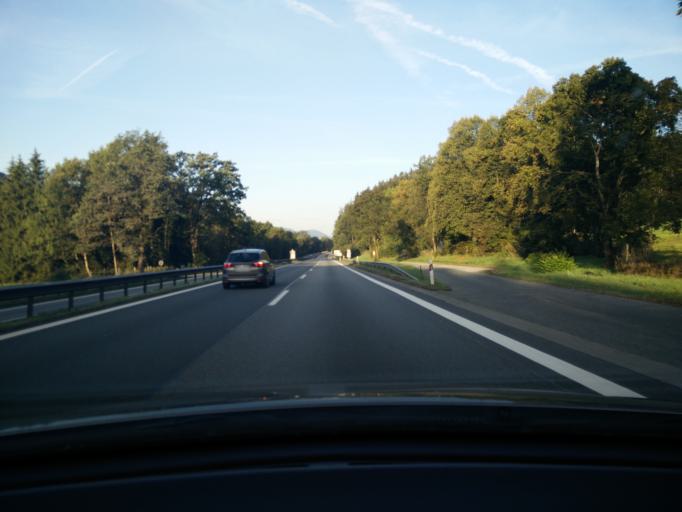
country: DE
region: Bavaria
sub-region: Upper Bavaria
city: Samerberg
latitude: 47.7975
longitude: 12.2263
